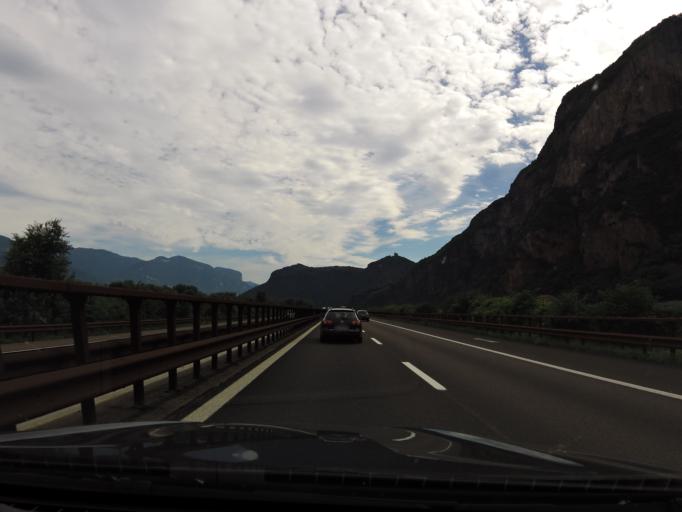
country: IT
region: Trentino-Alto Adige
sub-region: Bolzano
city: Vadena
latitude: 46.4022
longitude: 11.3004
